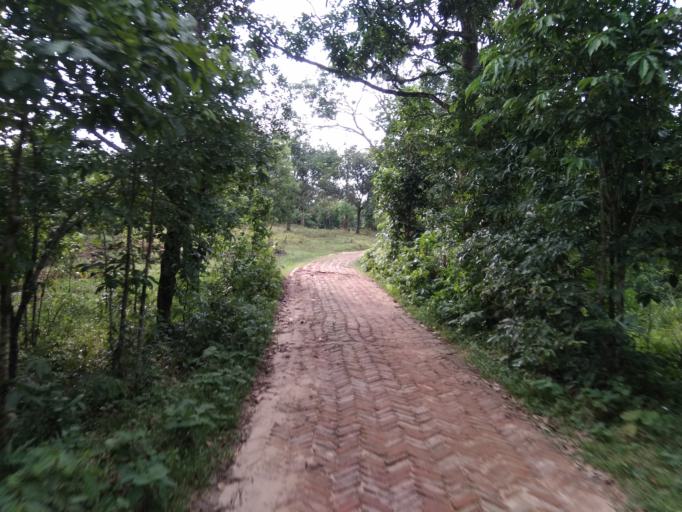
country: BD
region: Chittagong
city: Manikchari
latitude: 22.9297
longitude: 91.9124
